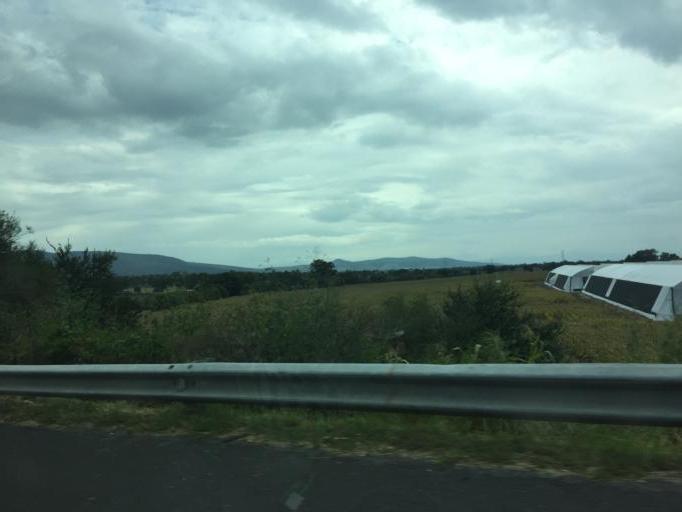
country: MX
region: Jalisco
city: Ocotlan
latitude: 20.3982
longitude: -102.7302
